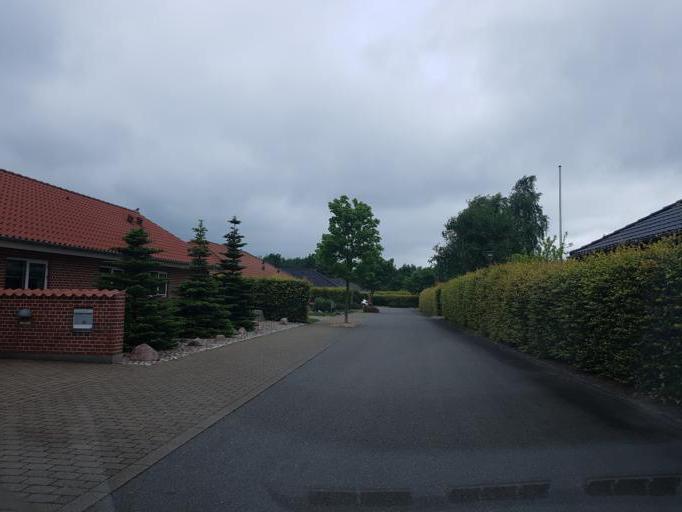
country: DK
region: South Denmark
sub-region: Varde Kommune
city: Varde
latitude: 55.6367
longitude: 8.4792
